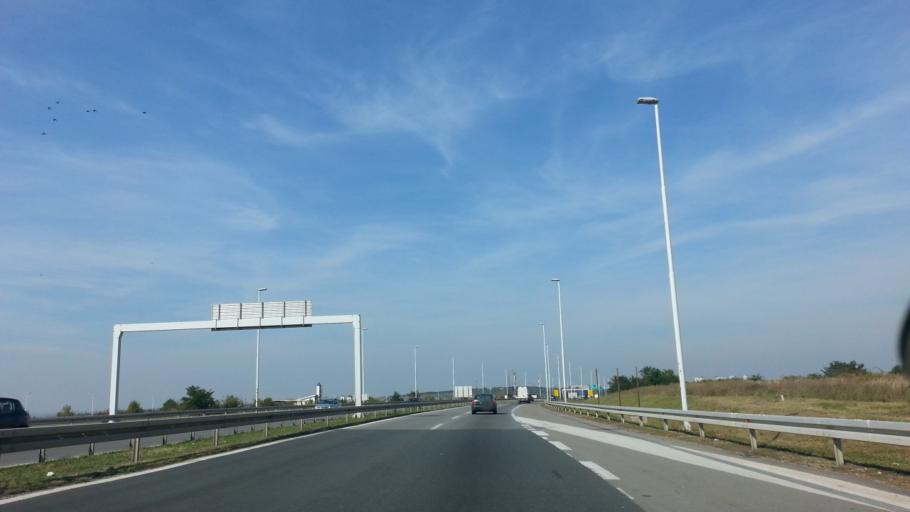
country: RS
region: Central Serbia
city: Sremcica
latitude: 44.7030
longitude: 20.4132
